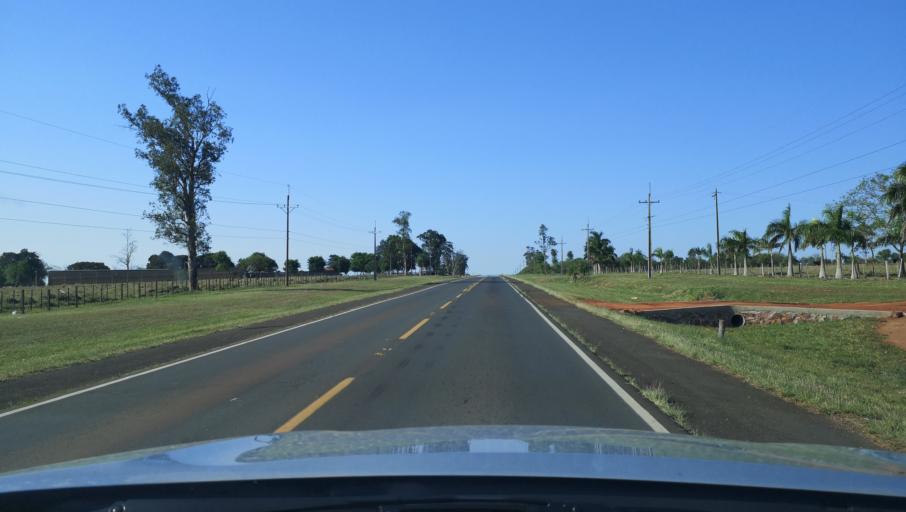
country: PY
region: Misiones
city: Santa Maria
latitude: -26.8260
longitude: -57.0289
